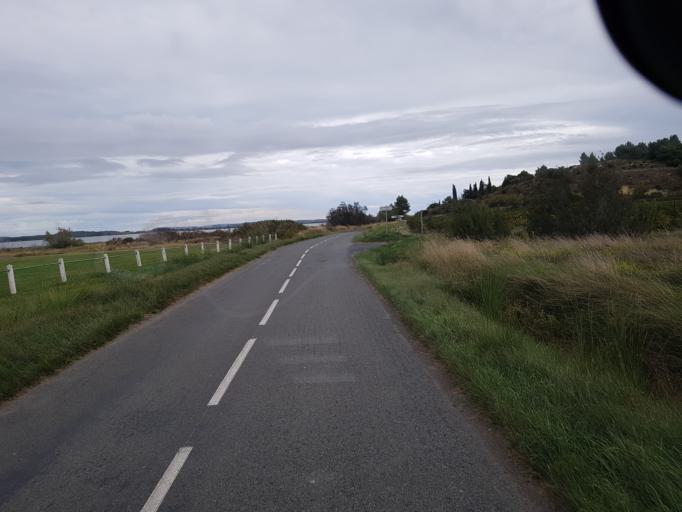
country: FR
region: Languedoc-Roussillon
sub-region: Departement de l'Aude
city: Narbonne
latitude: 43.1352
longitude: 2.9839
